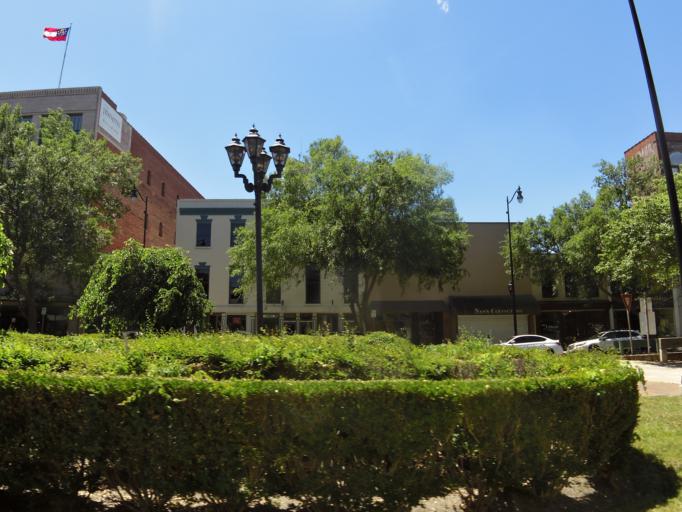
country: US
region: Georgia
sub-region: Richmond County
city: Augusta
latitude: 33.4765
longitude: -81.9687
